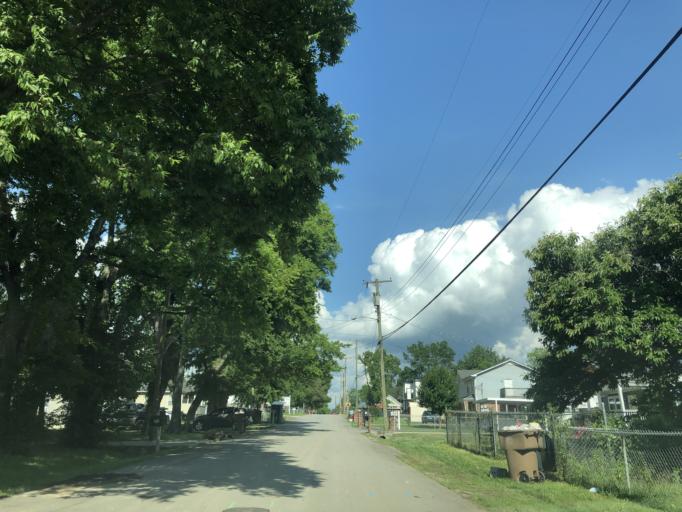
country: US
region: Tennessee
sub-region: Davidson County
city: Nashville
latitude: 36.2074
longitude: -86.7656
